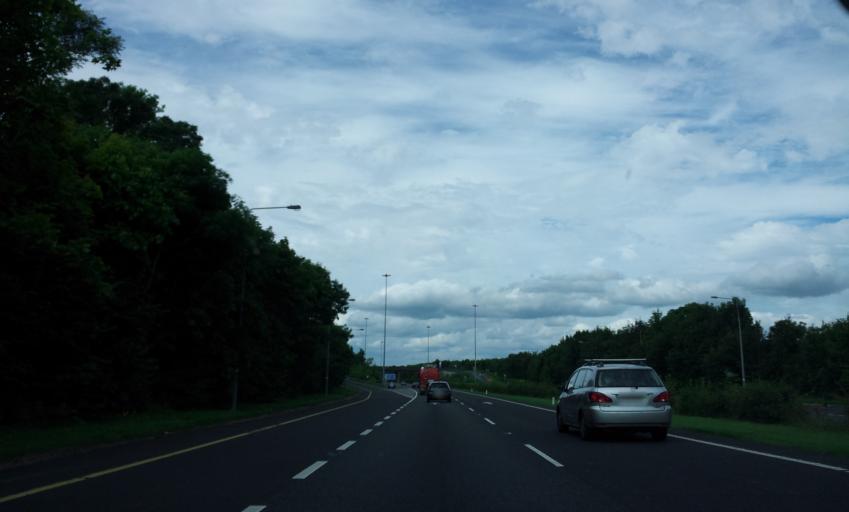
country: IE
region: Leinster
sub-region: Kildare
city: Old Kilcullen
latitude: 53.1172
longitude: -6.7539
